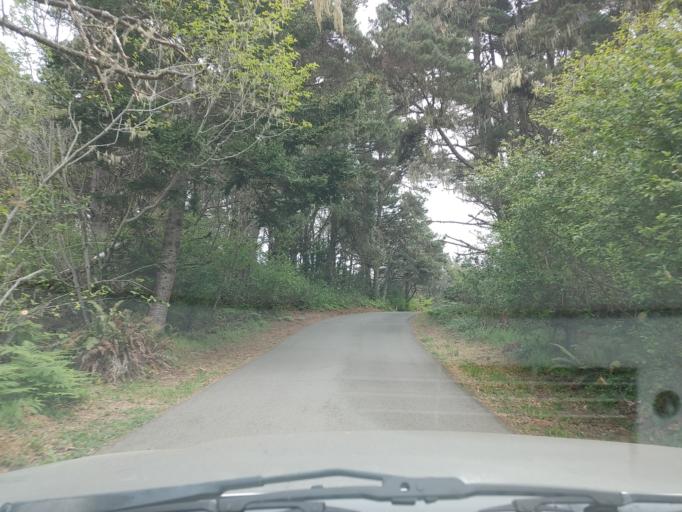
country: US
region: California
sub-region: Mendocino County
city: Fort Bragg
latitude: 39.3303
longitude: -123.8073
